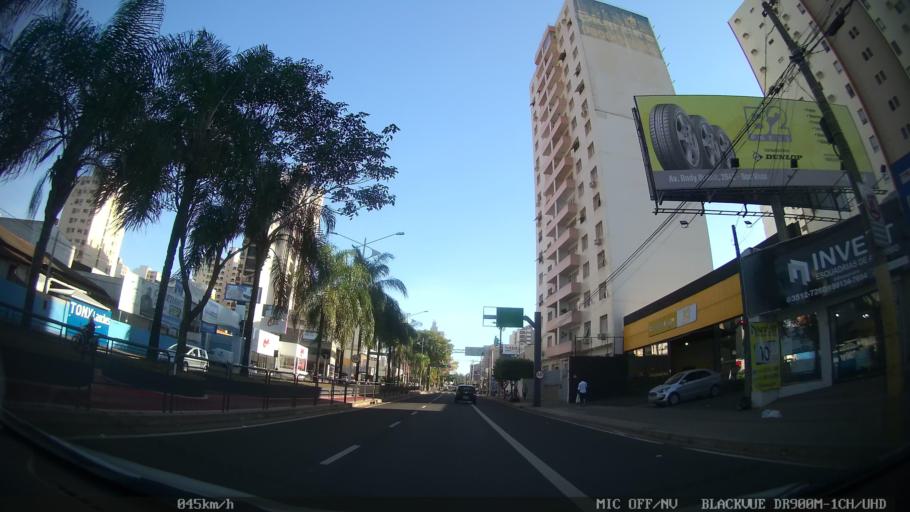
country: BR
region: Sao Paulo
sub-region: Sao Jose Do Rio Preto
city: Sao Jose do Rio Preto
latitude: -20.8085
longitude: -49.3820
